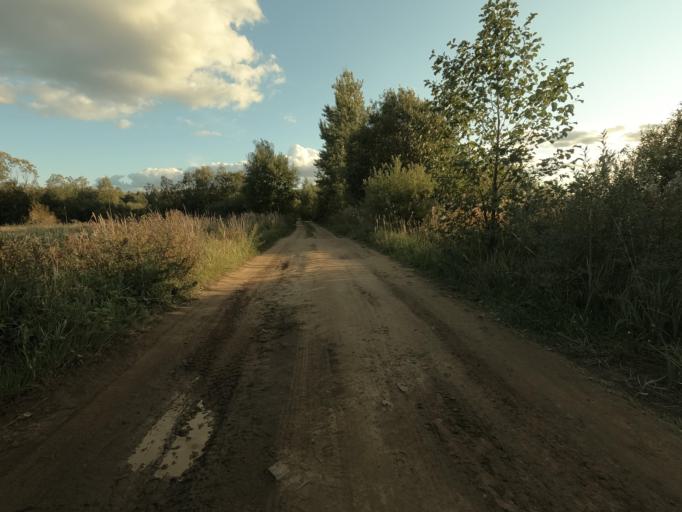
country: RU
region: Leningrad
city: Otradnoye
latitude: 59.8562
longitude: 30.7964
